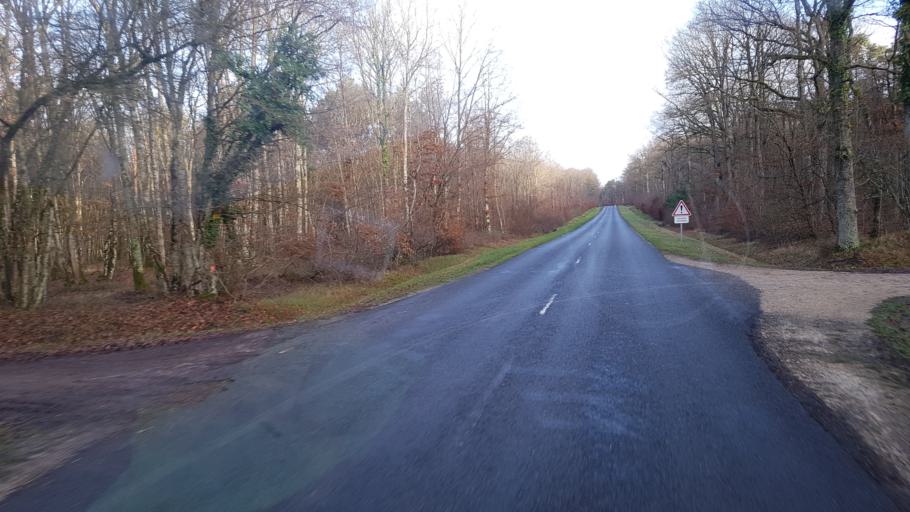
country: FR
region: Centre
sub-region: Departement du Loiret
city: Chilleurs-aux-Bois
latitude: 48.0396
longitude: 2.2129
